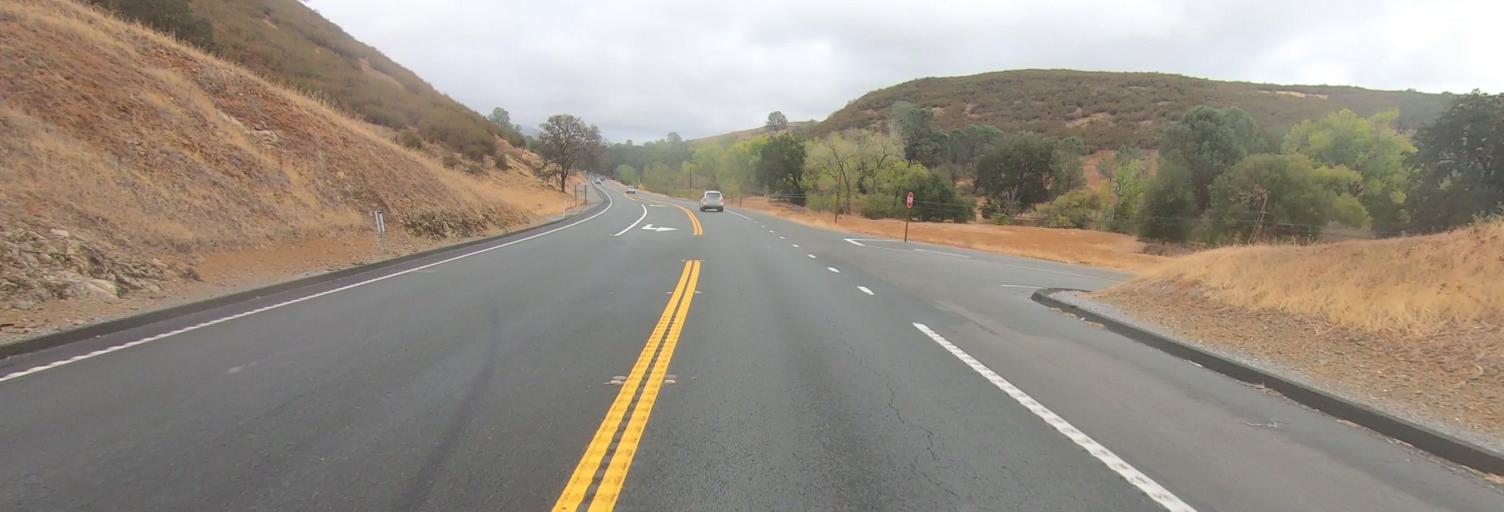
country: US
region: California
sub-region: Calaveras County
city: Valley Springs
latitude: 38.1971
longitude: -120.8012
